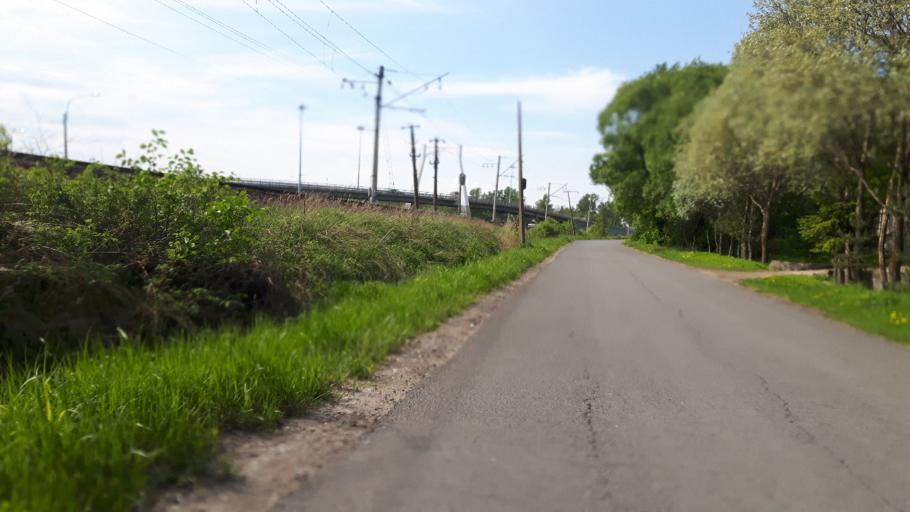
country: RU
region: Leningrad
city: Gorskaya
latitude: 60.0343
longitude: 29.9831
